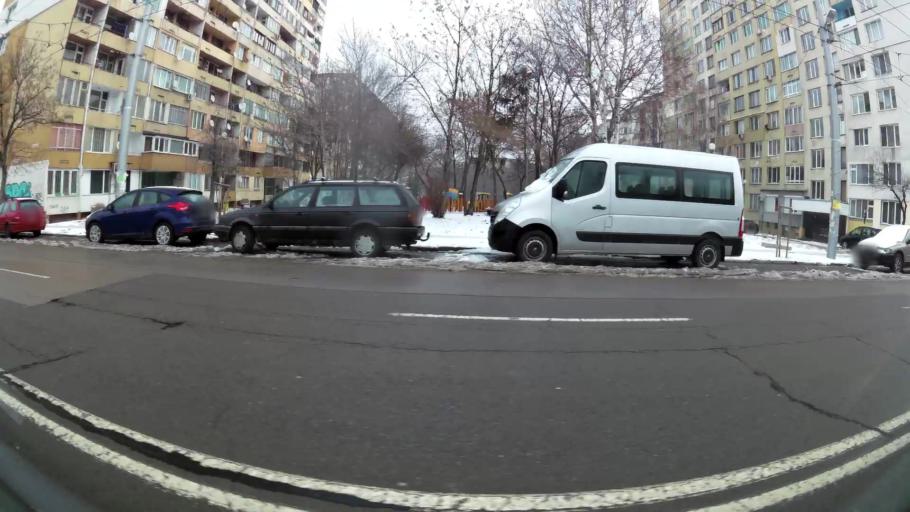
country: BG
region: Sofia-Capital
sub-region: Stolichna Obshtina
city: Sofia
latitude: 42.7121
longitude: 23.3087
